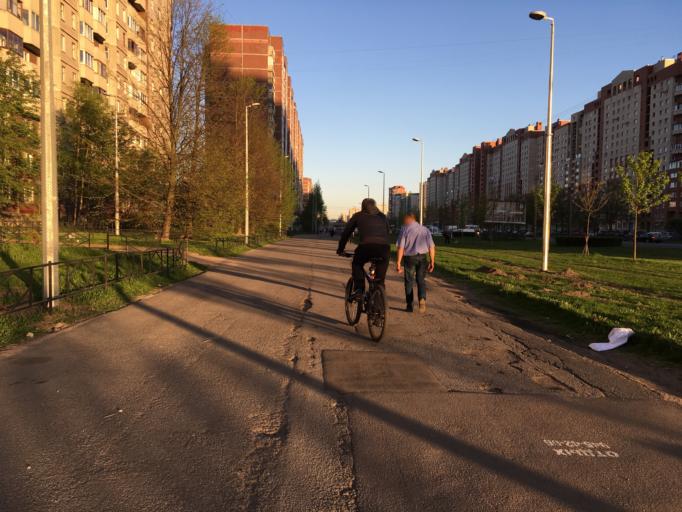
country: RU
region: Leningrad
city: Untolovo
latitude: 60.0245
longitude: 30.2408
